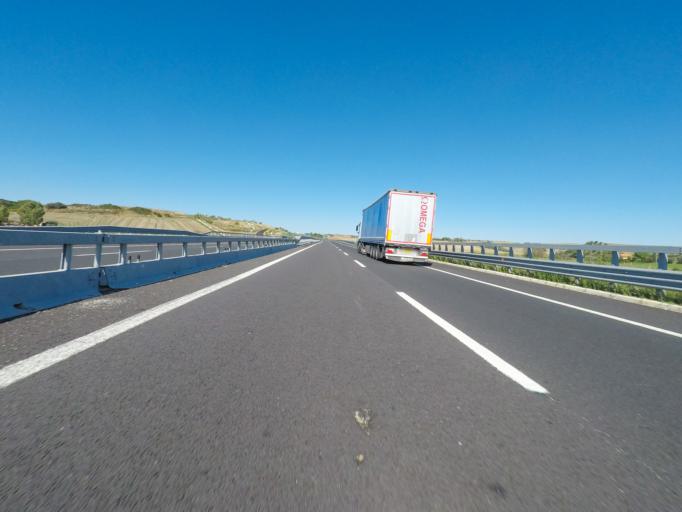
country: IT
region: Latium
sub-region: Citta metropolitana di Roma Capitale
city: Aurelia
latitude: 42.2003
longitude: 11.7856
